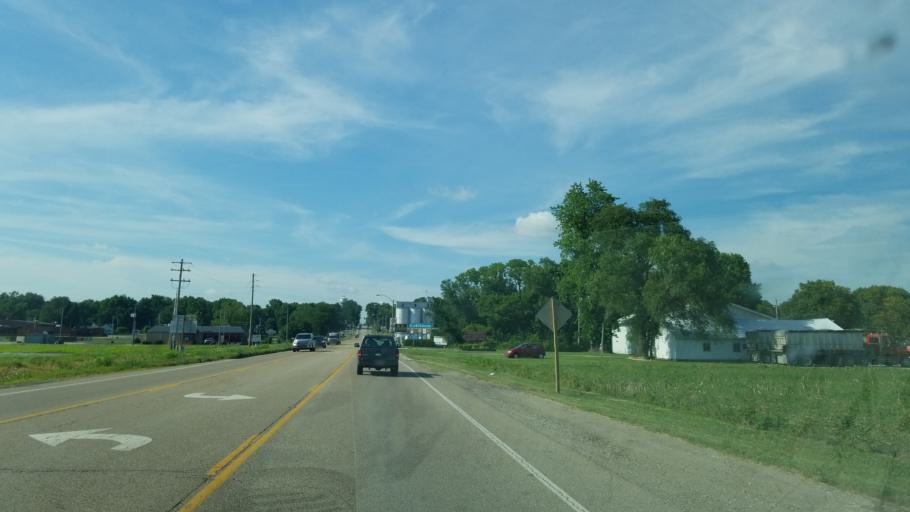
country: US
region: Illinois
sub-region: Saint Clair County
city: Lebanon
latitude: 38.5968
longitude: -89.8076
